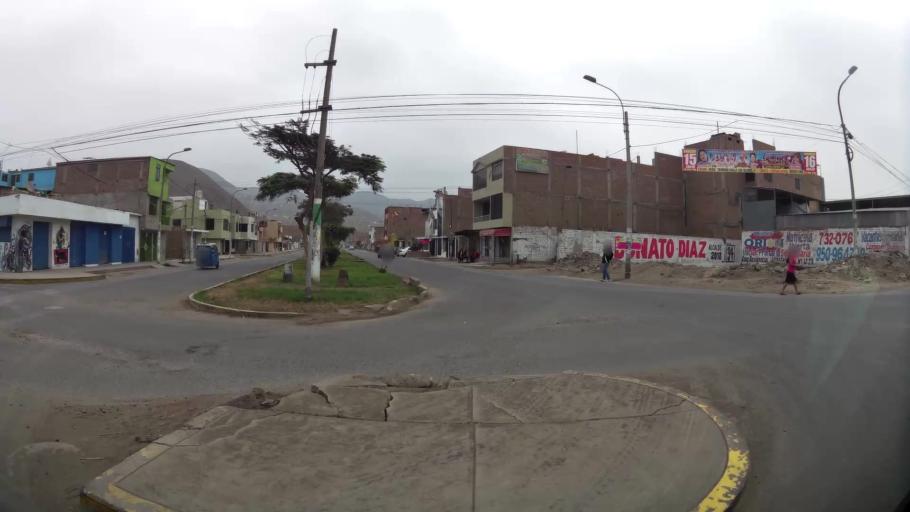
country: PE
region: Lima
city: Ventanilla
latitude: -11.9296
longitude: -77.0788
